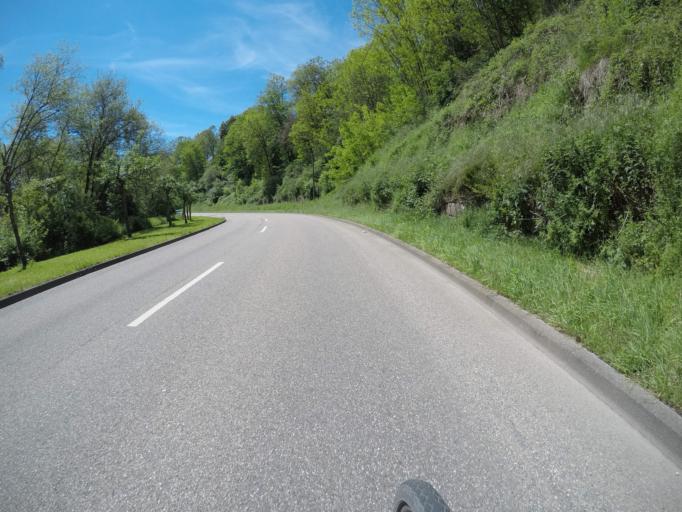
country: DE
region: Baden-Wuerttemberg
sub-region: Karlsruhe Region
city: Heimsheim
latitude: 48.7939
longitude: 8.8330
